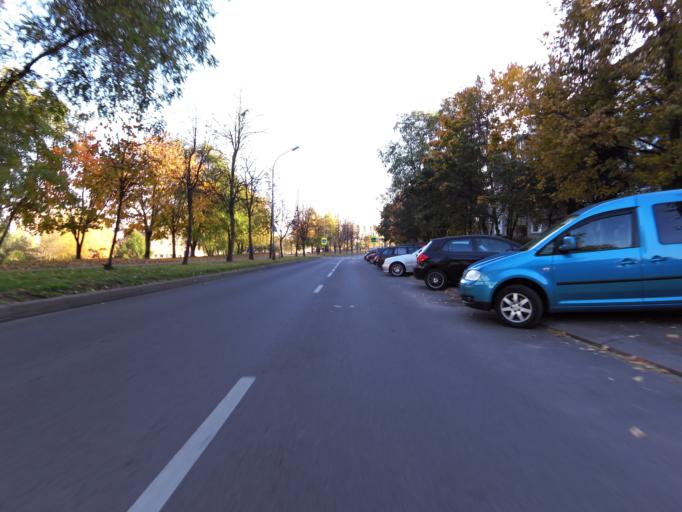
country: LT
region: Vilnius County
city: Pasilaiciai
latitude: 54.7342
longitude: 25.2288
